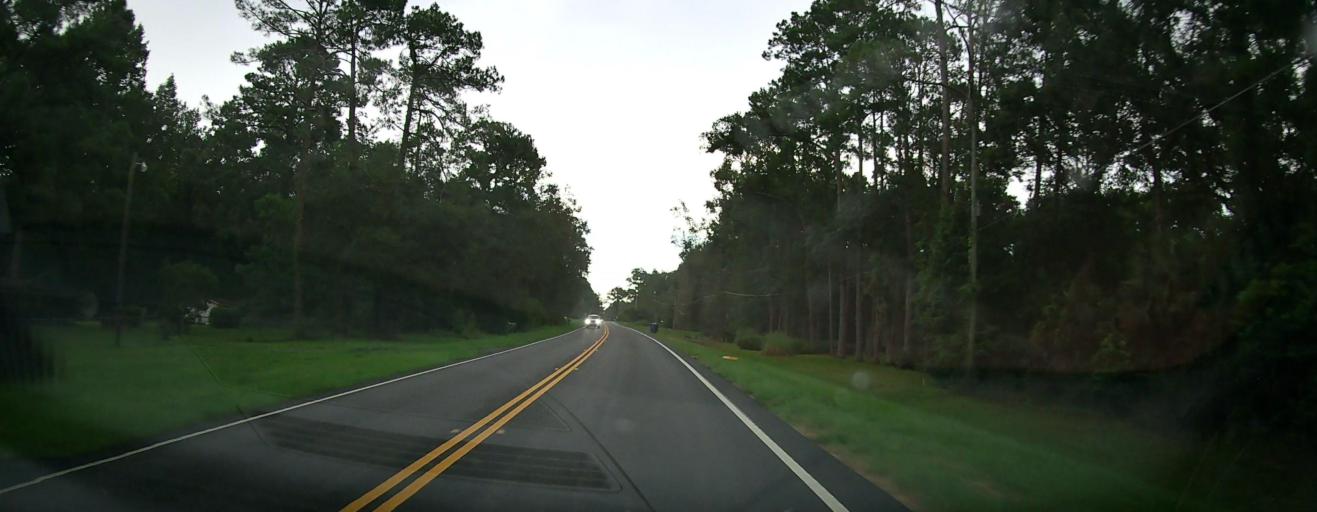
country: US
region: Georgia
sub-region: Glynn County
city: Dock Junction
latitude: 31.2930
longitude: -81.6941
